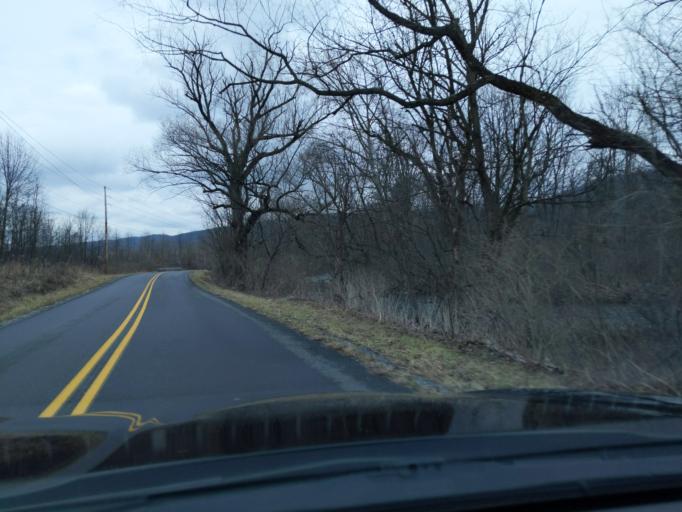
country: US
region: Pennsylvania
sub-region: Blair County
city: Tipton
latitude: 40.6280
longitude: -78.3076
